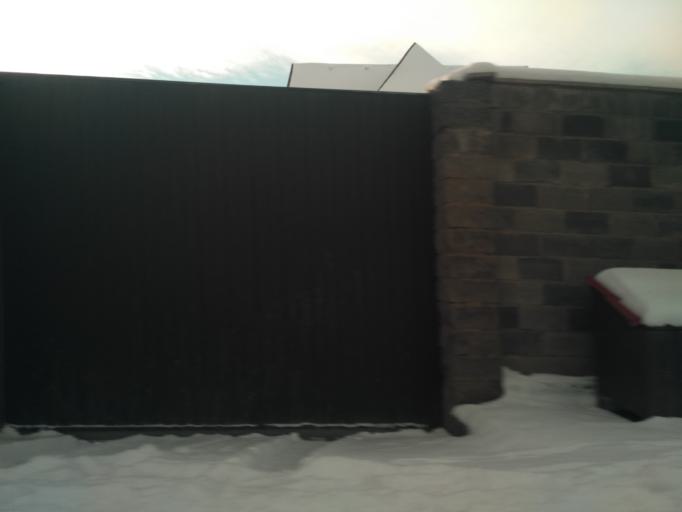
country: KZ
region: Almaty Qalasy
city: Almaty
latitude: 43.2173
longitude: 76.7656
